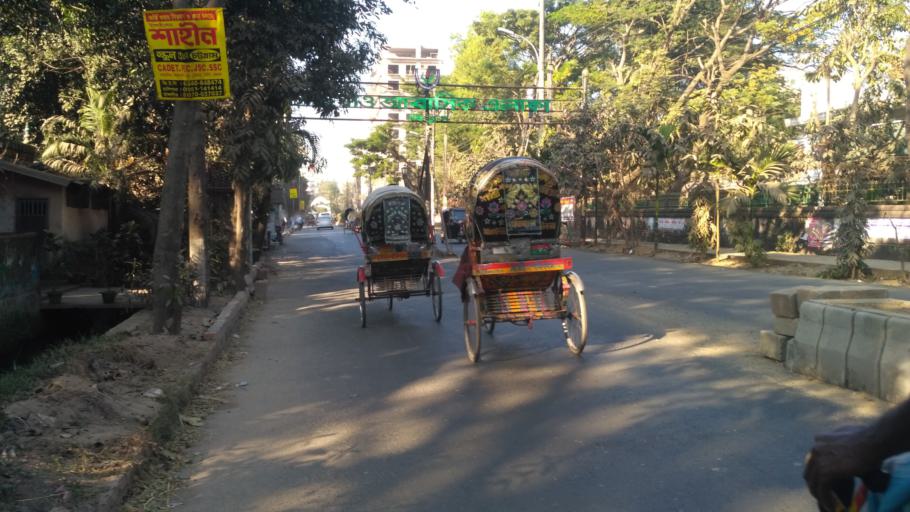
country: BD
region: Chittagong
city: Chittagong
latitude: 22.3752
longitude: 91.8470
